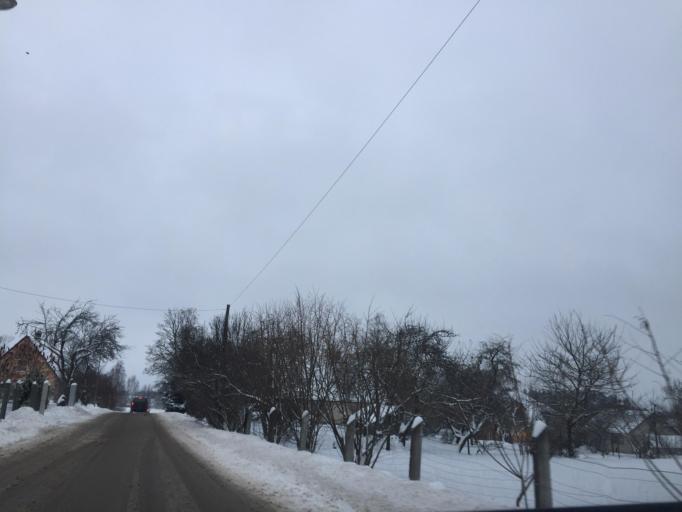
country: LV
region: Smiltene
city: Smiltene
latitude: 57.4172
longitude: 25.8926
